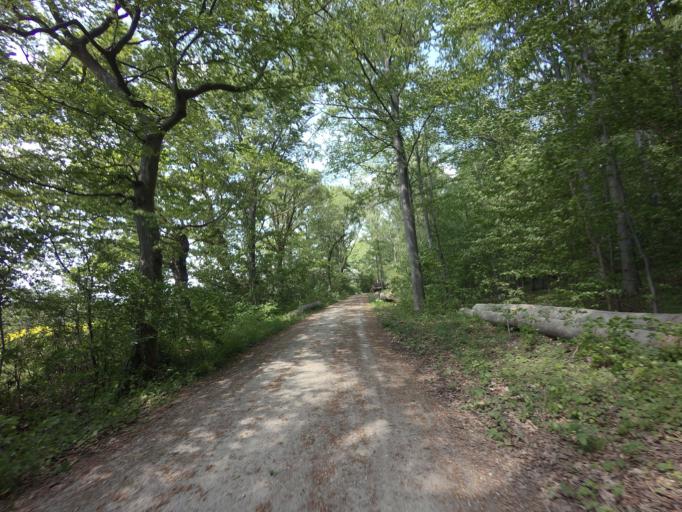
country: DE
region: Lower Saxony
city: Diekholzen
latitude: 52.1420
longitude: 9.8910
